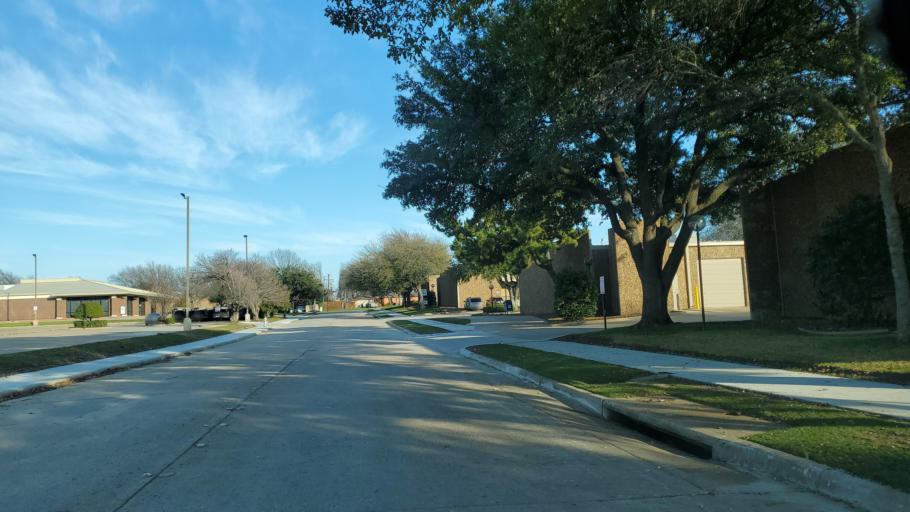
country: US
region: Texas
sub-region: Collin County
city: Plano
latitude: 33.0263
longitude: -96.7068
